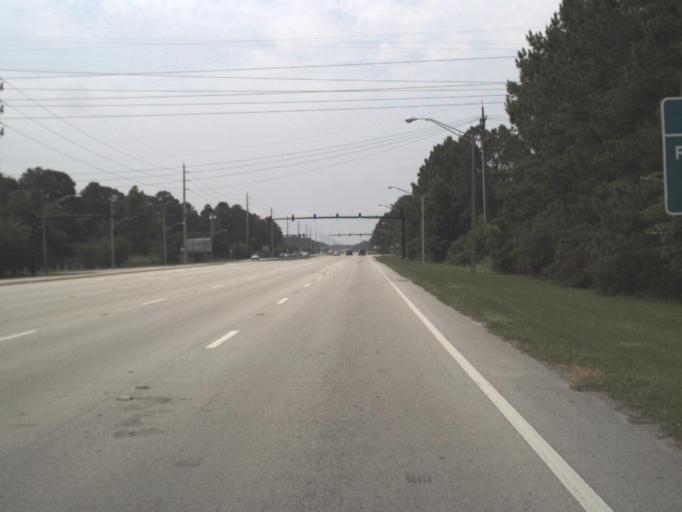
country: US
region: Florida
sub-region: Clay County
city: Orange Park
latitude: 30.2219
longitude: -81.7019
